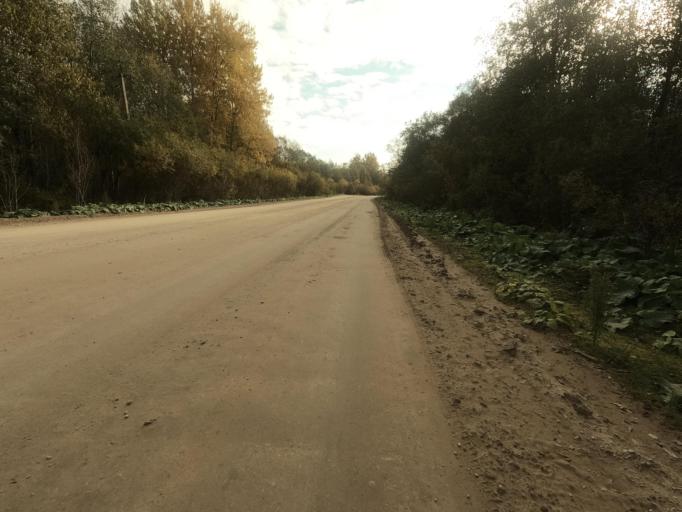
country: RU
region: Novgorod
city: Batetskiy
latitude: 58.8020
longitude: 30.6502
